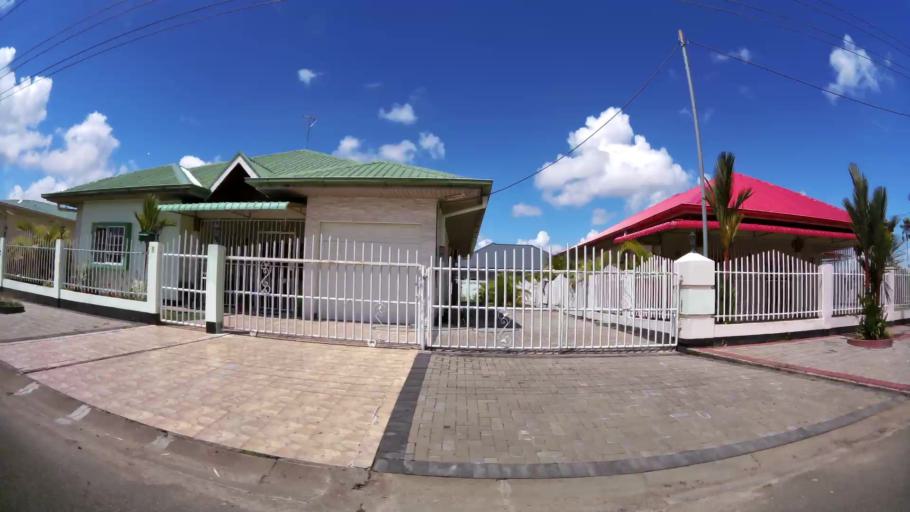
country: SR
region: Paramaribo
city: Paramaribo
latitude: 5.8627
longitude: -55.1451
